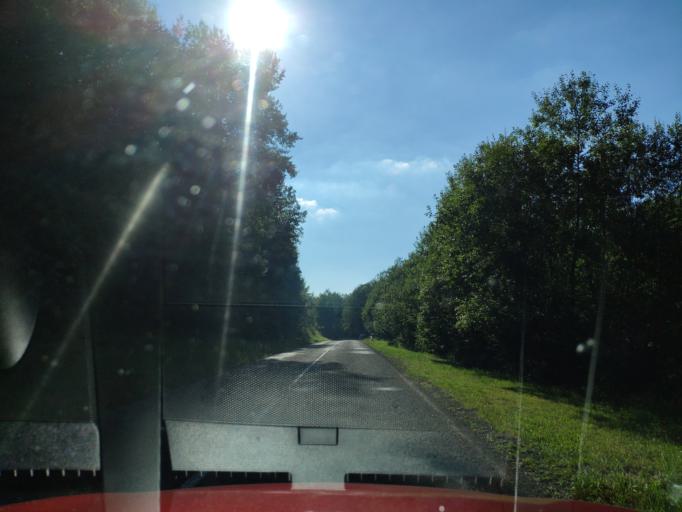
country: SK
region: Presovsky
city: Snina
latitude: 49.0449
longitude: 22.2743
